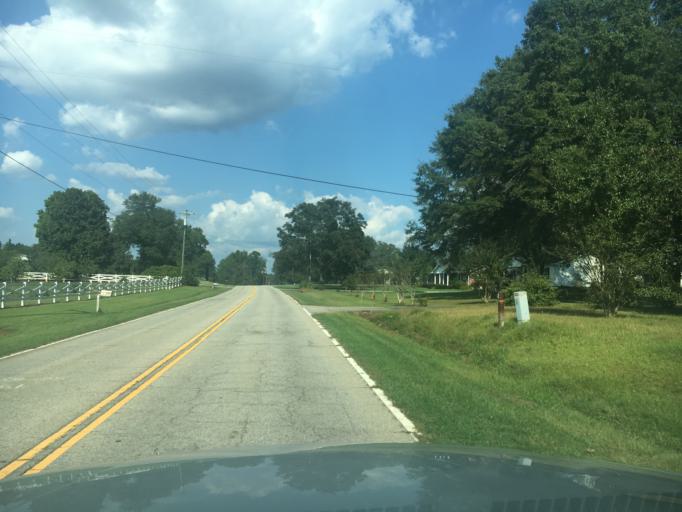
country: US
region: South Carolina
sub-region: Anderson County
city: Pendleton
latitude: 34.6675
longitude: -82.7636
